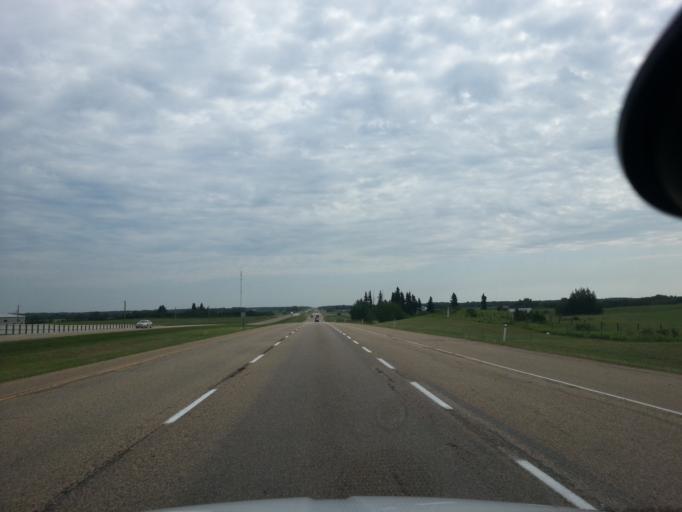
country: CA
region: Alberta
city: Fort Saskatchewan
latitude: 53.5699
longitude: -113.0355
